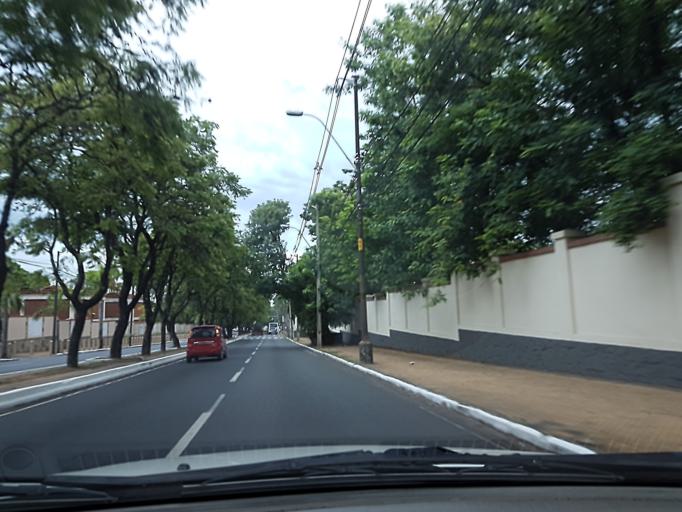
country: PY
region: Asuncion
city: Asuncion
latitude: -25.2945
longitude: -57.6037
